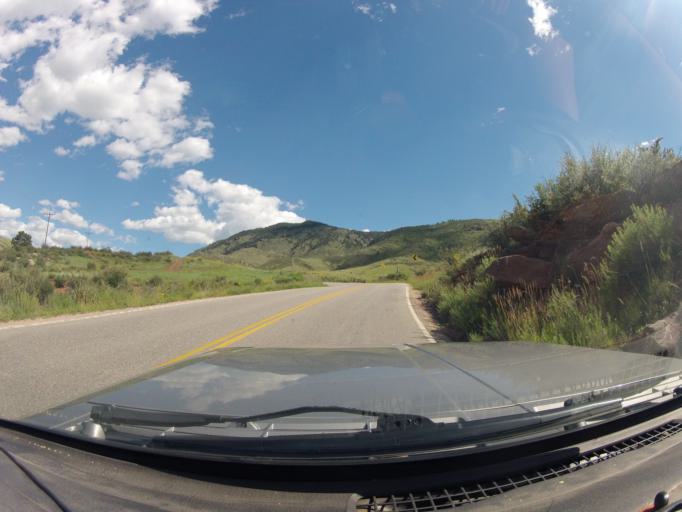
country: US
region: Colorado
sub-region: Larimer County
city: Laporte
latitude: 40.5223
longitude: -105.2582
